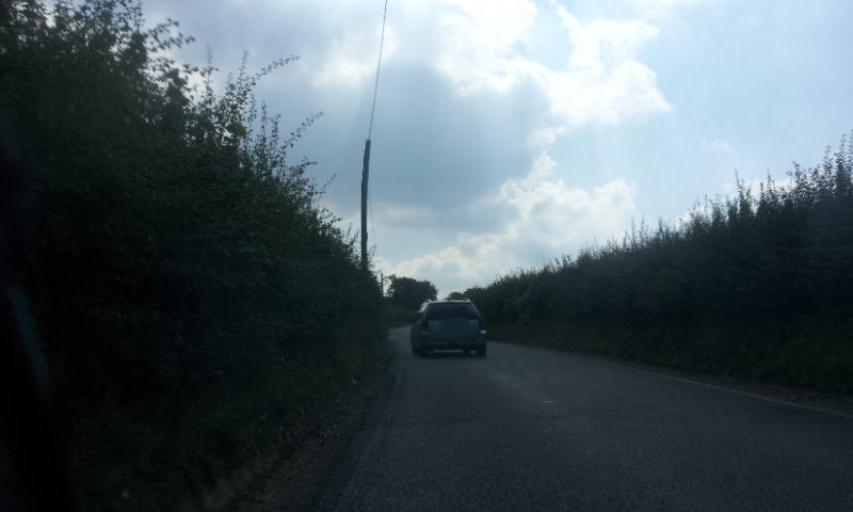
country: GB
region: England
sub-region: Kent
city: Boxley
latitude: 51.3123
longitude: 0.5492
